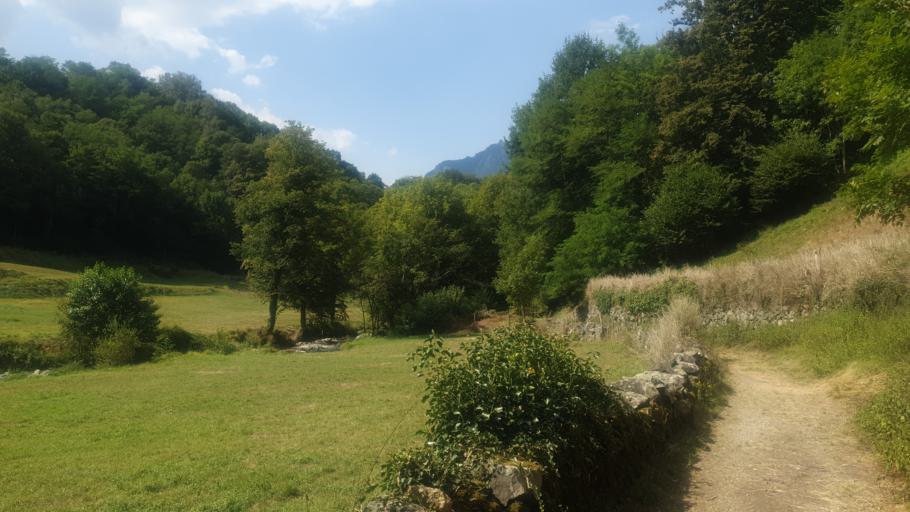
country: FR
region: Aquitaine
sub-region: Departement des Pyrenees-Atlantiques
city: Arette
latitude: 42.9969
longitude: -0.5902
